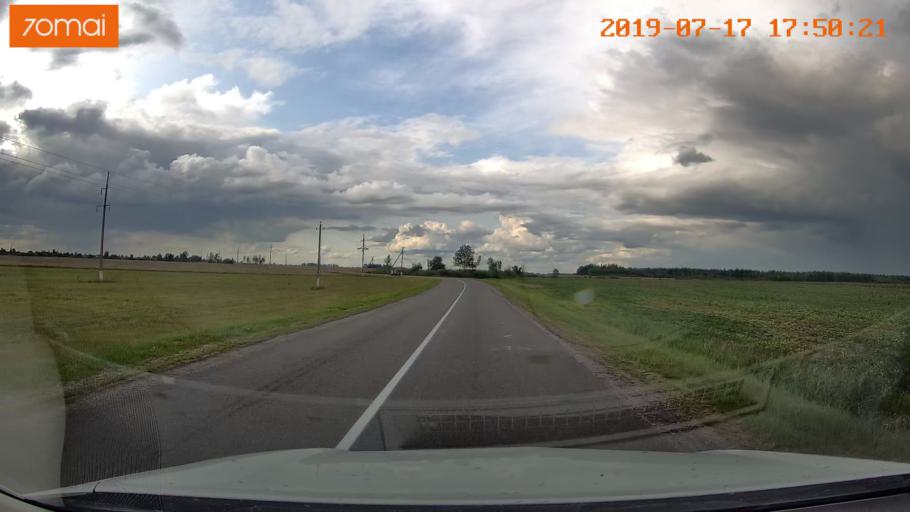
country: BY
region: Mogilev
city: Hlusha
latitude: 53.1388
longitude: 28.8032
